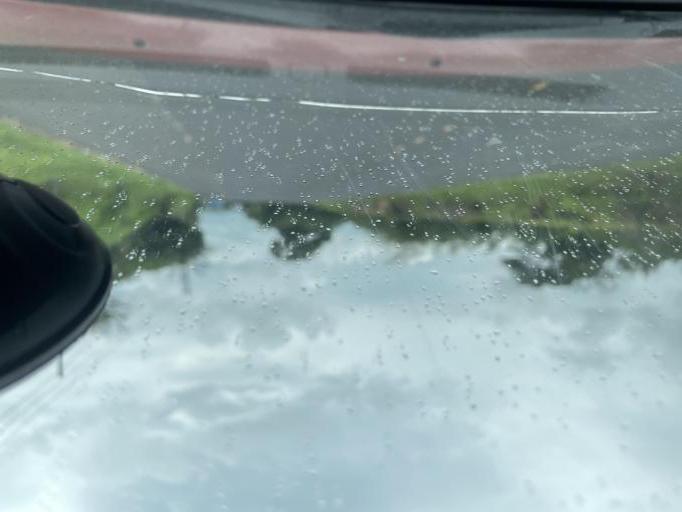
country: SV
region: San Miguel
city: Chirilagua
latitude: 13.3348
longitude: -88.1471
